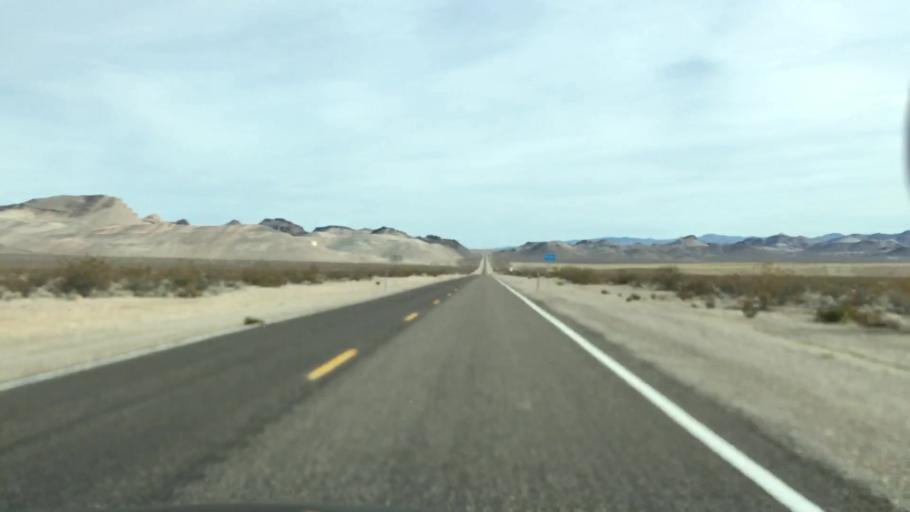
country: US
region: Nevada
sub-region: Nye County
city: Beatty
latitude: 36.8730
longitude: -116.8271
